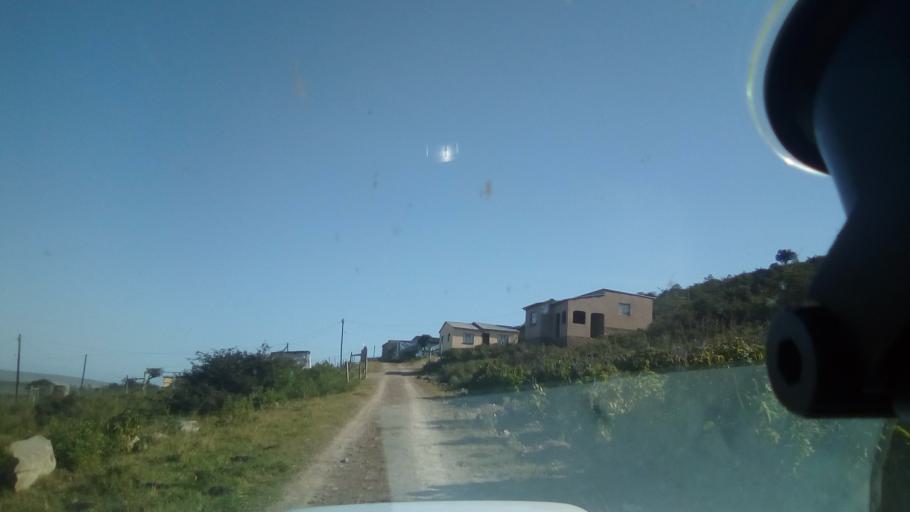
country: ZA
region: Eastern Cape
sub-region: Buffalo City Metropolitan Municipality
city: Bhisho
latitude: -32.8121
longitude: 27.3510
